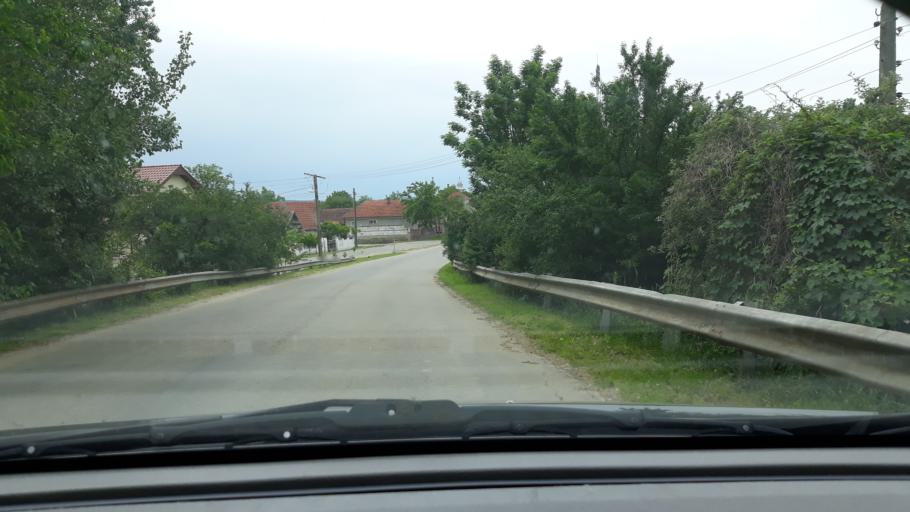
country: RO
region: Bihor
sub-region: Comuna Osorheiu
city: Osorheiu
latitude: 47.0597
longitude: 22.0430
